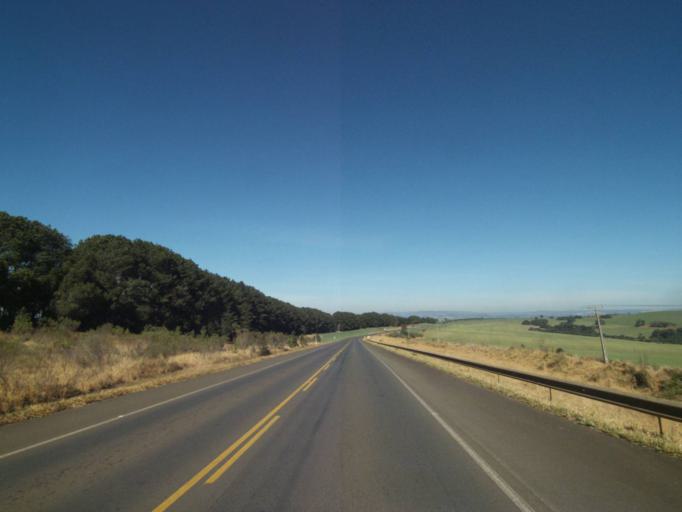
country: BR
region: Parana
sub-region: Tibagi
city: Tibagi
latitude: -24.4120
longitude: -50.3645
